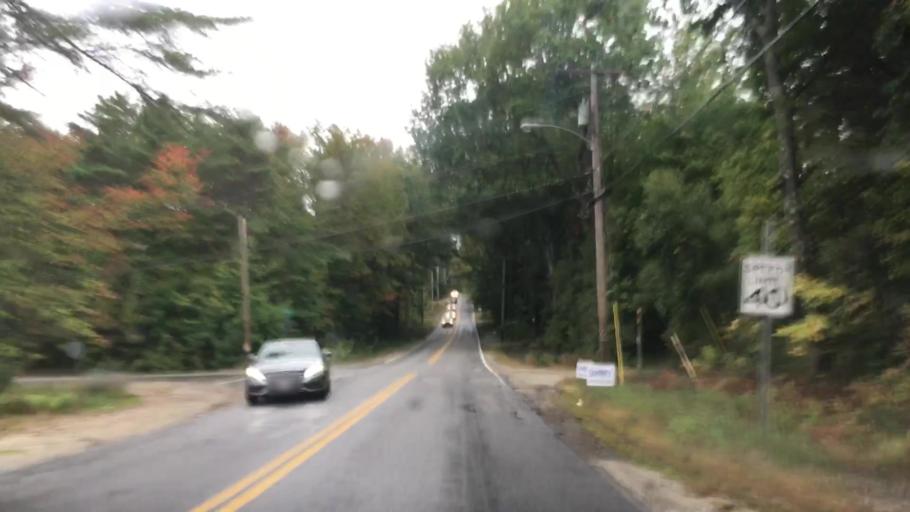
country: US
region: Maine
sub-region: Cumberland County
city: New Gloucester
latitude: 43.9277
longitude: -70.3697
